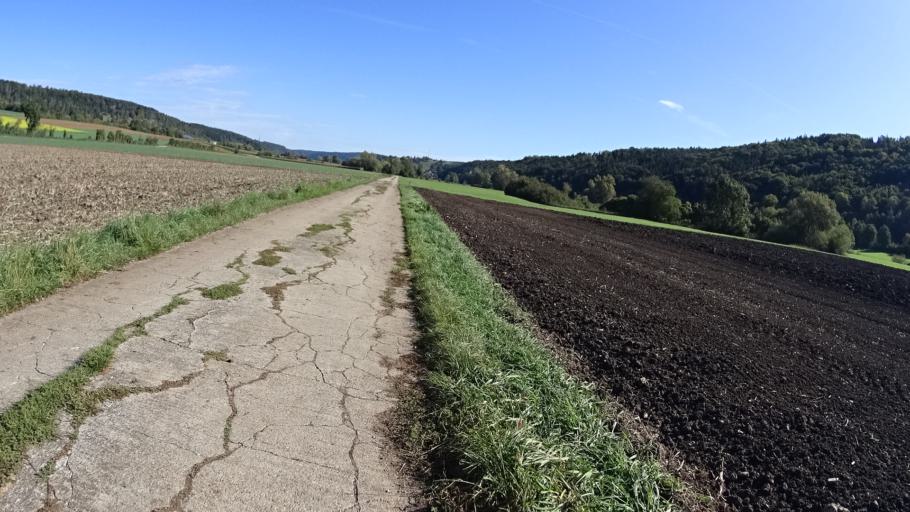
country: DE
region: Bavaria
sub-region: Upper Bavaria
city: Eichstaett
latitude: 48.8788
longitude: 11.2398
